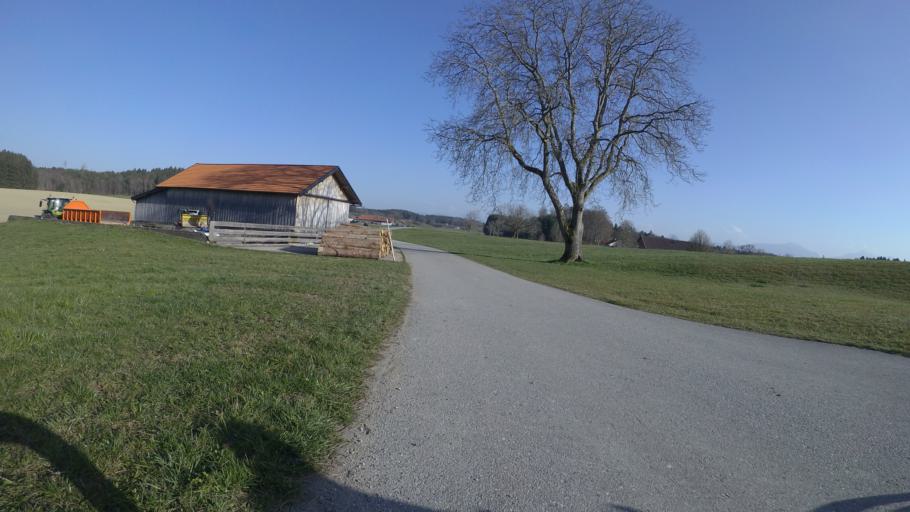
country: DE
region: Bavaria
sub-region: Upper Bavaria
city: Traunreut
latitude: 47.9349
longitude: 12.5605
